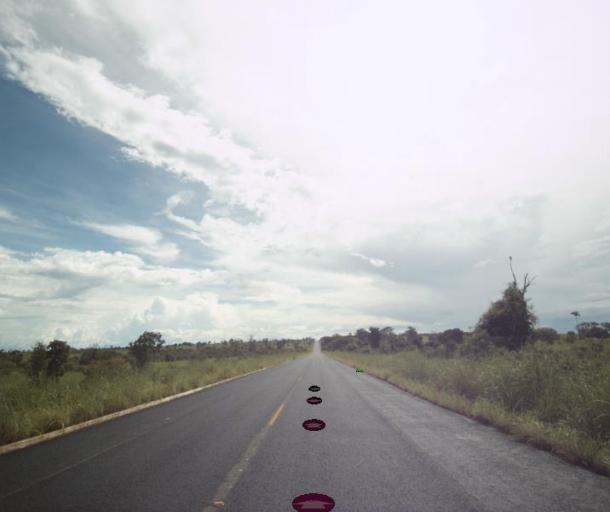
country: BR
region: Goias
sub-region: Sao Miguel Do Araguaia
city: Sao Miguel do Araguaia
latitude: -13.3016
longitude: -50.2858
